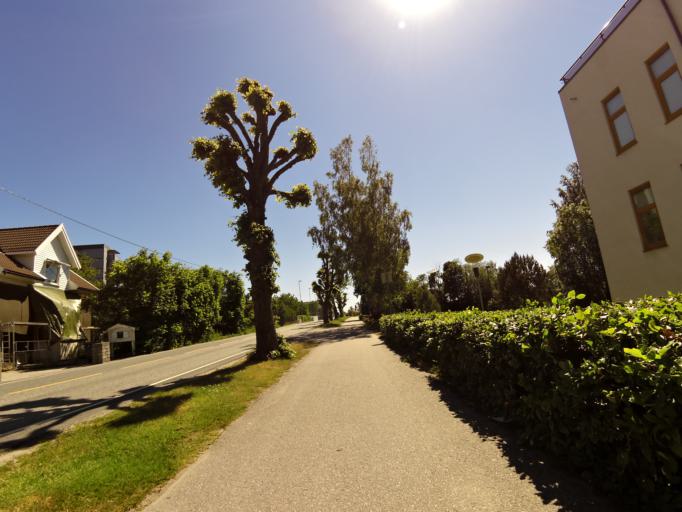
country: NO
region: Vest-Agder
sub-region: Kristiansand
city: Kristiansand
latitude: 58.1565
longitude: 8.0110
